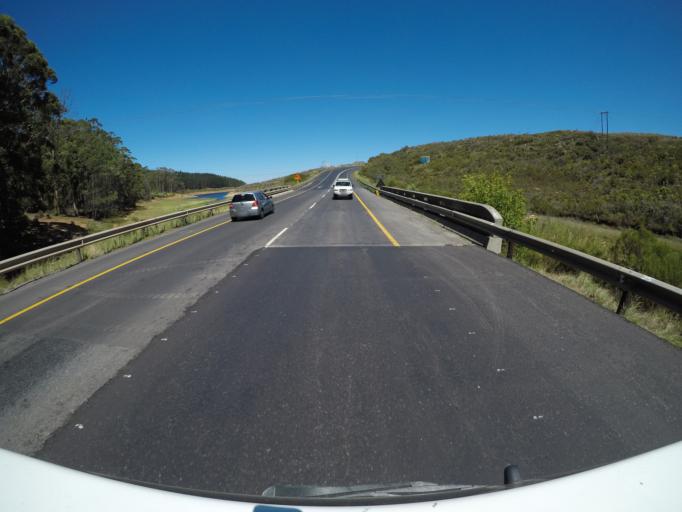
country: ZA
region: Western Cape
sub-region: Overberg District Municipality
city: Grabouw
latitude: -34.1528
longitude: 18.9429
